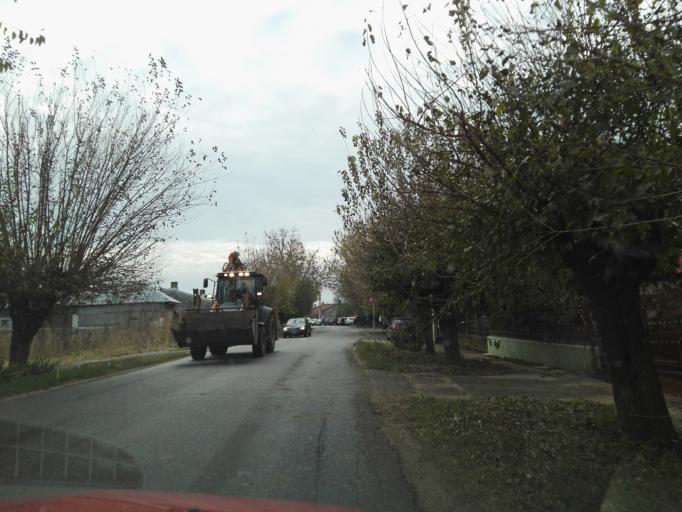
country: RO
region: Ilfov
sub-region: Comuna Magurele
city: Alunisu
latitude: 44.3362
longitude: 26.0623
